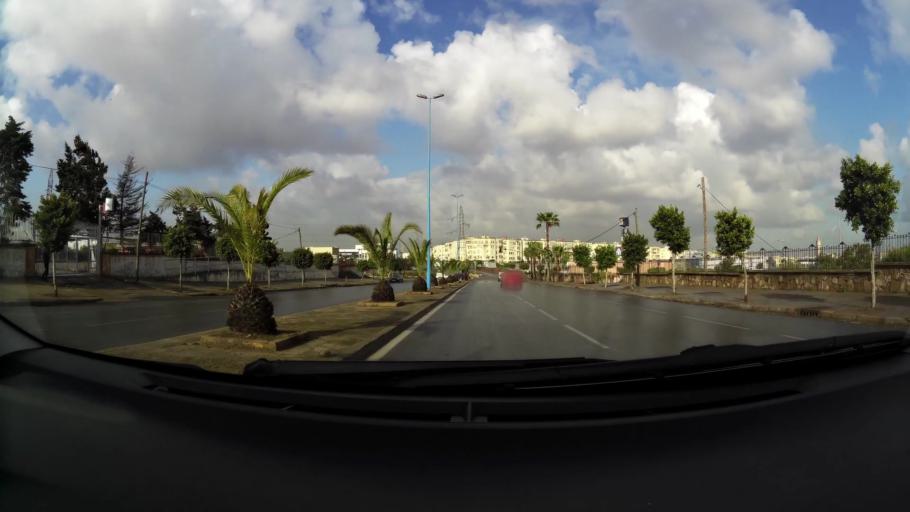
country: MA
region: Grand Casablanca
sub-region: Mediouna
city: Tit Mellil
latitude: 33.5950
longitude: -7.5286
